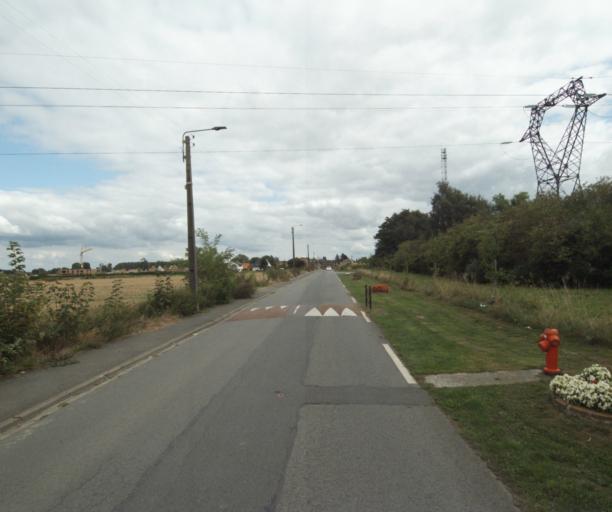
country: FR
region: Nord-Pas-de-Calais
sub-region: Departement du Nord
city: Anstaing
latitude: 50.6075
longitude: 3.1836
